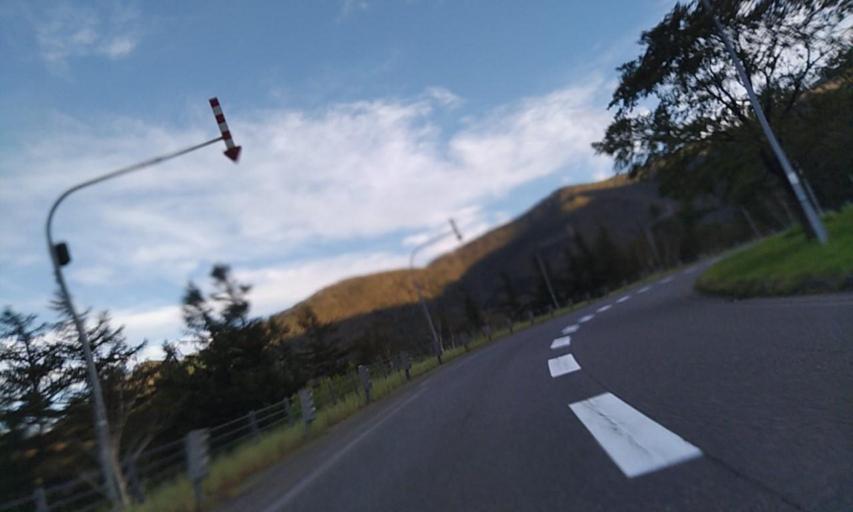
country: JP
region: Hokkaido
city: Otofuke
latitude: 42.9579
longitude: 142.7944
